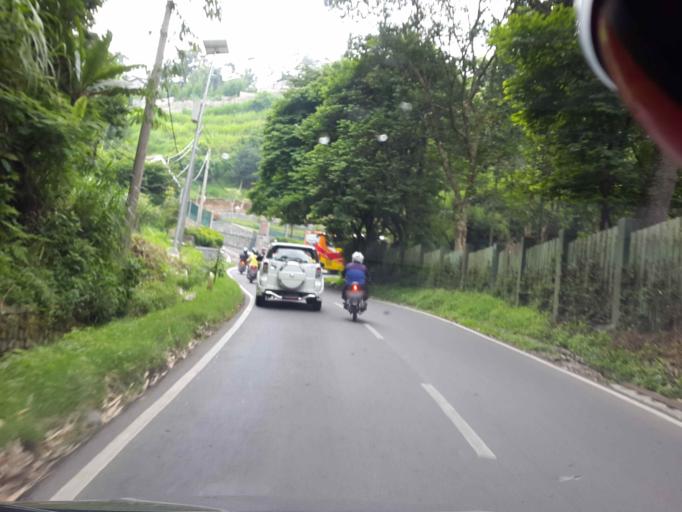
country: ID
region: West Java
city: Lembang
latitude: -6.8221
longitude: 107.6059
